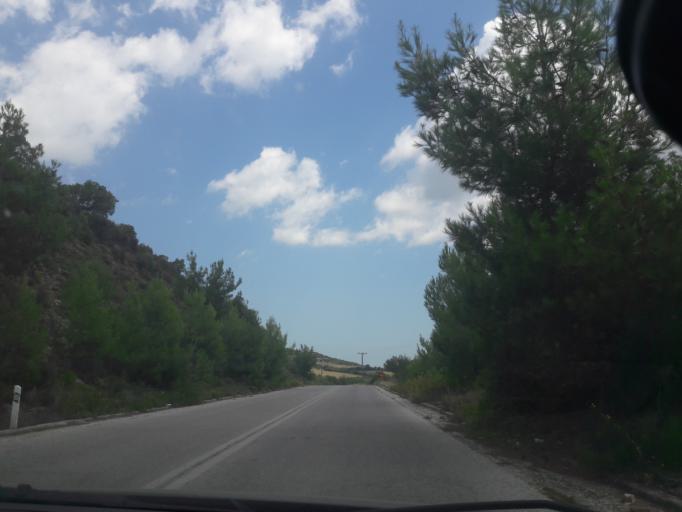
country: GR
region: Central Macedonia
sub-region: Nomos Chalkidikis
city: Polygyros
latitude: 40.3689
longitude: 23.5080
